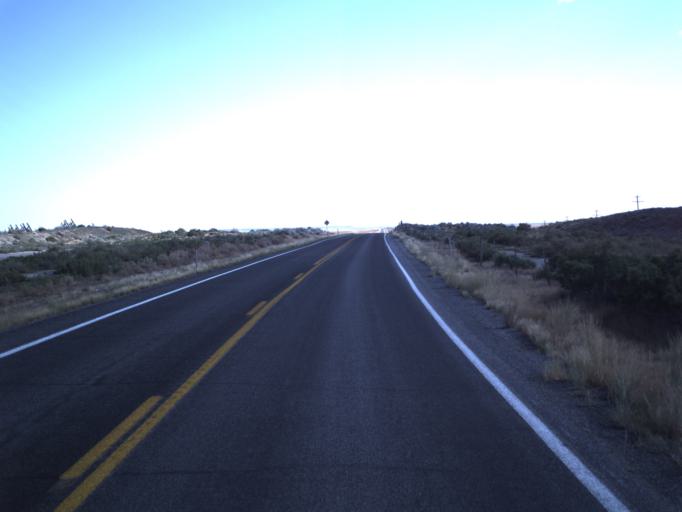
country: US
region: Utah
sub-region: Millard County
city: Delta
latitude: 38.9563
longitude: -112.8049
